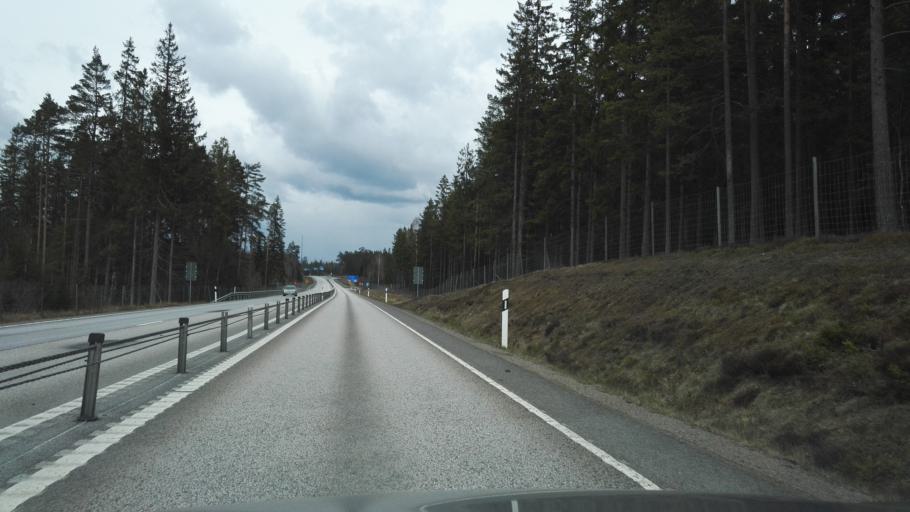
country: SE
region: Kronoberg
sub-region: Vaxjo Kommun
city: Braas
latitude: 57.0108
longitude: 15.0476
